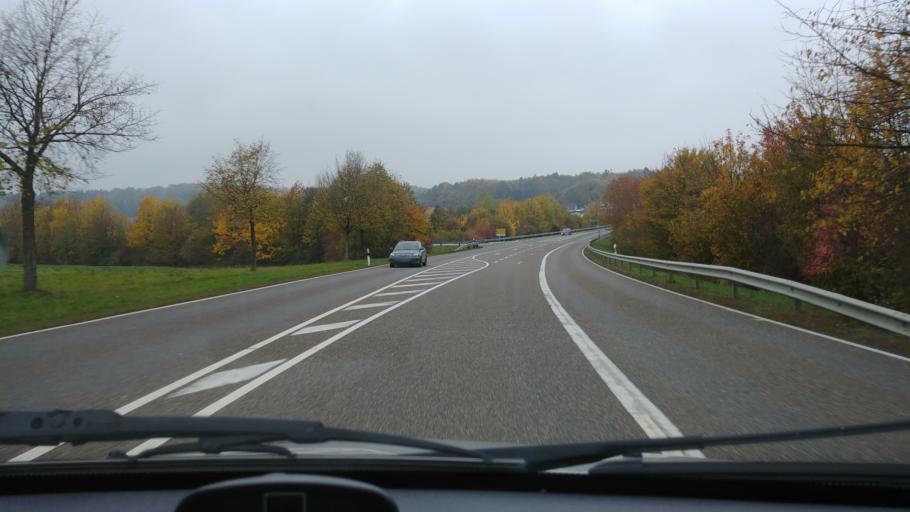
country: DE
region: Rheinland-Pfalz
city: Willmenrod
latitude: 50.5541
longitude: 7.9646
